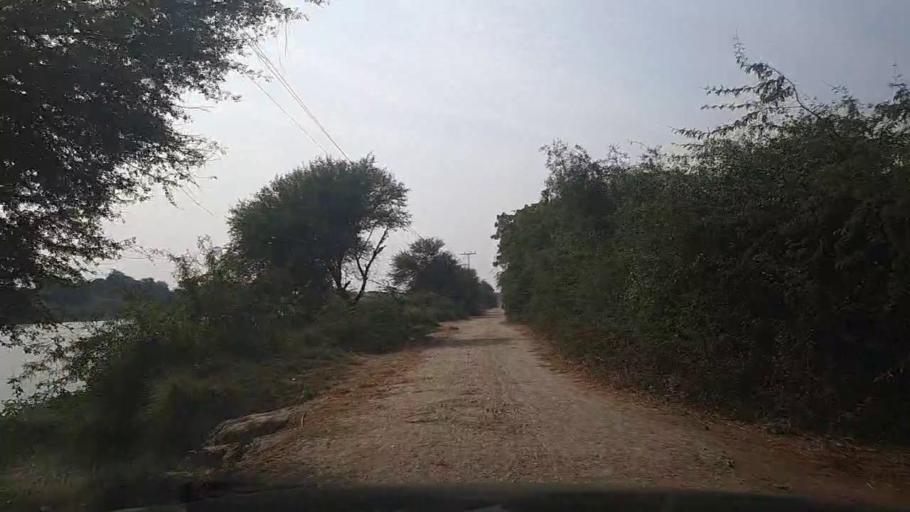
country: PK
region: Sindh
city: Bulri
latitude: 24.9643
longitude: 68.3290
